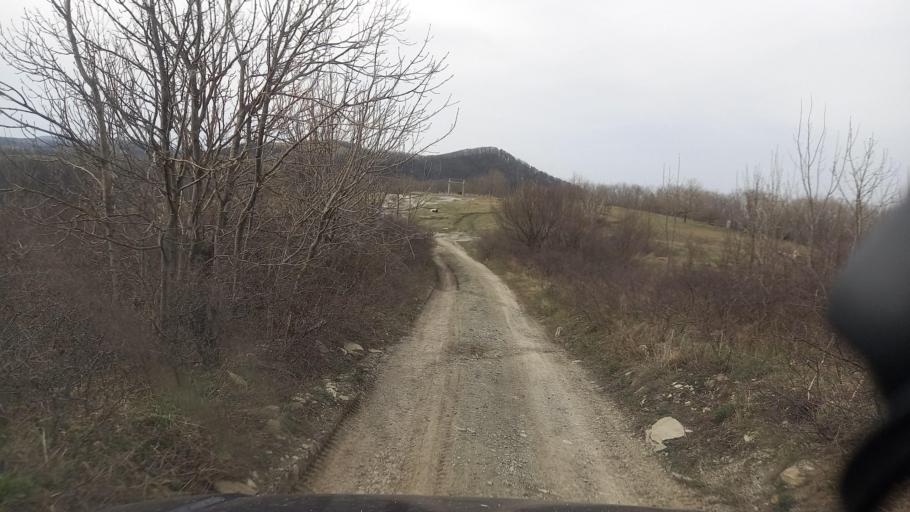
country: RU
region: Krasnodarskiy
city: Divnomorskoye
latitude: 44.6106
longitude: 38.2344
